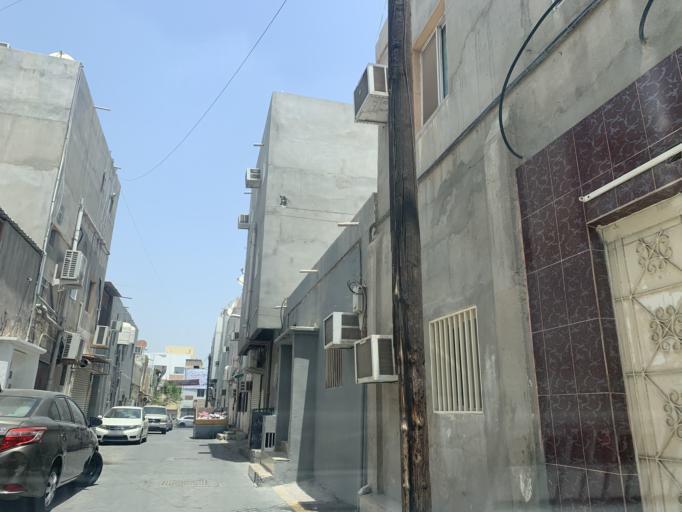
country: BH
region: Central Governorate
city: Madinat Hamad
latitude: 26.1449
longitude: 50.4972
